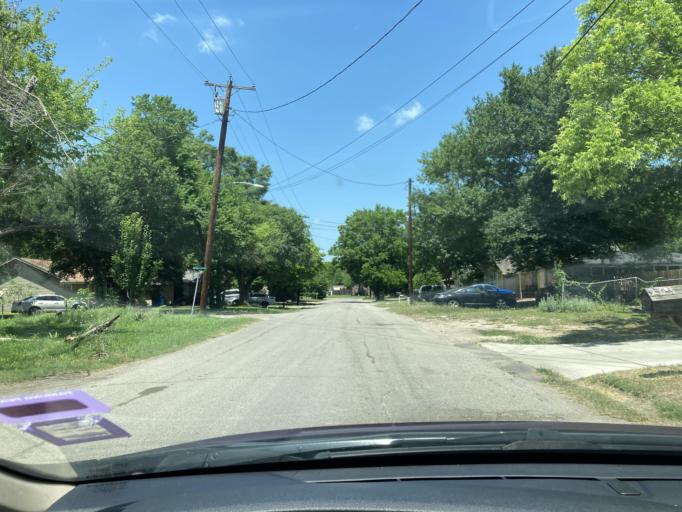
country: US
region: Texas
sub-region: Navarro County
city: Corsicana
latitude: 32.0827
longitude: -96.4663
